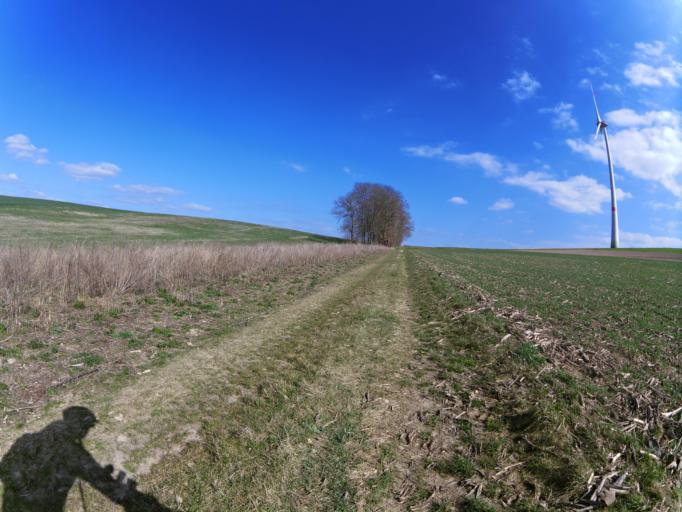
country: DE
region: Bavaria
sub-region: Regierungsbezirk Unterfranken
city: Dettelbach
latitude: 49.8330
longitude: 10.1580
